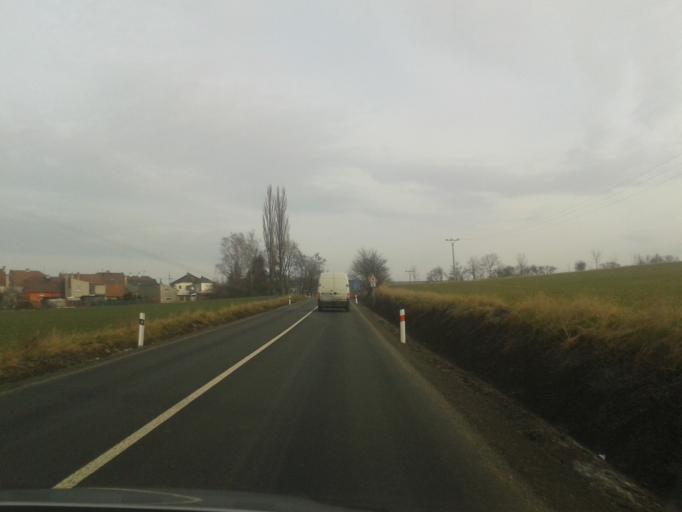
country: CZ
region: Olomoucky
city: Smrzice
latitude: 49.5133
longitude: 17.1035
